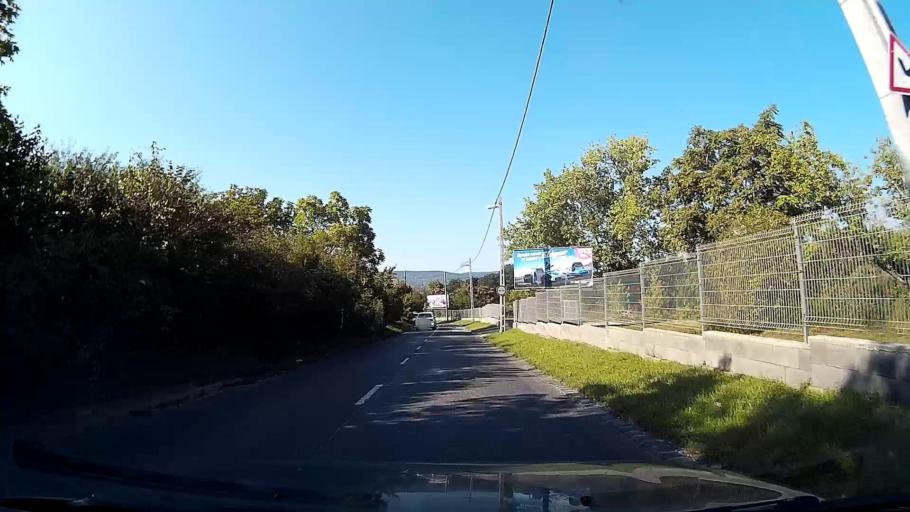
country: HU
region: Pest
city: Budaors
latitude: 47.4346
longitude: 18.9795
